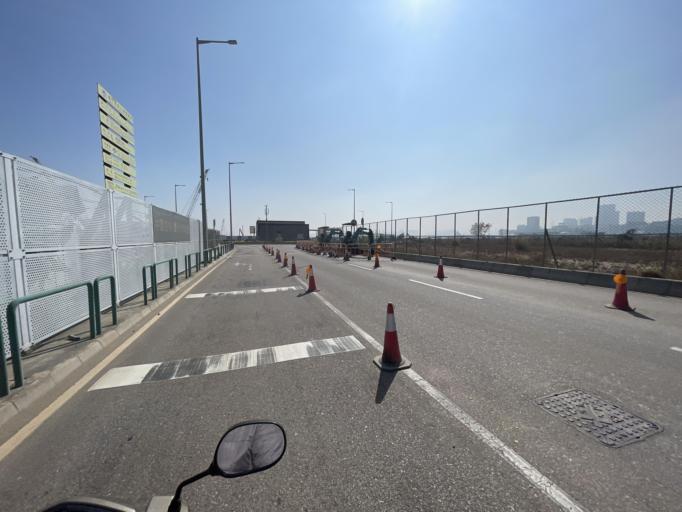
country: MO
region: Macau
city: Macau
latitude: 22.2046
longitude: 113.5654
